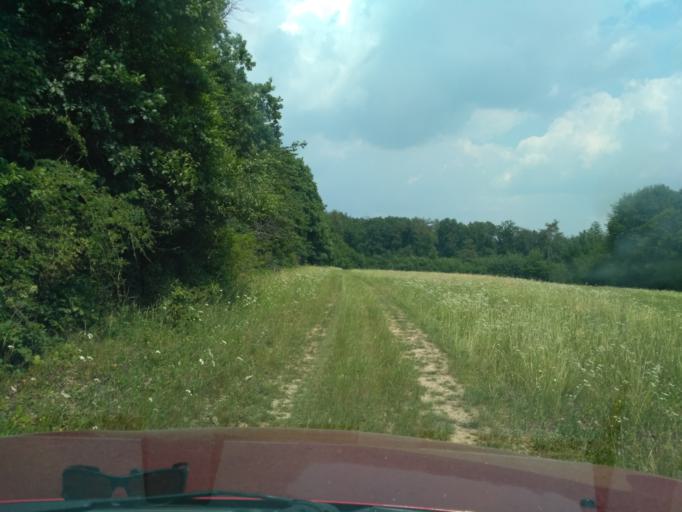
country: SK
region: Kosicky
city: Moldava nad Bodvou
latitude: 48.6305
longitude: 21.0435
